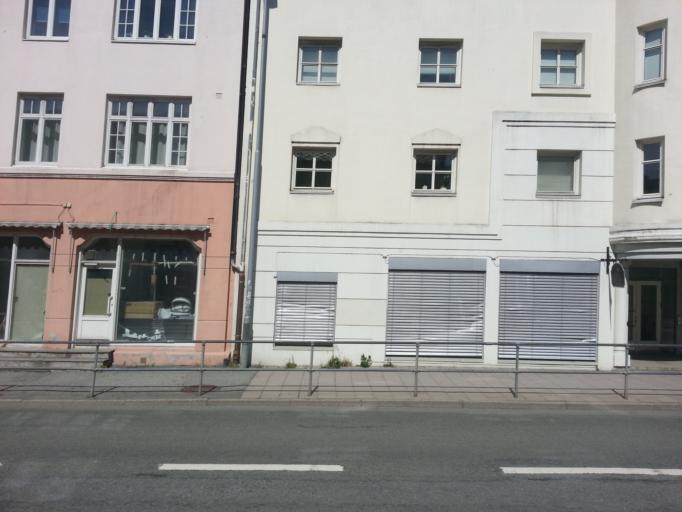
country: NO
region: Sor-Trondelag
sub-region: Trondheim
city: Trondheim
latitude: 63.4361
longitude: 10.4211
